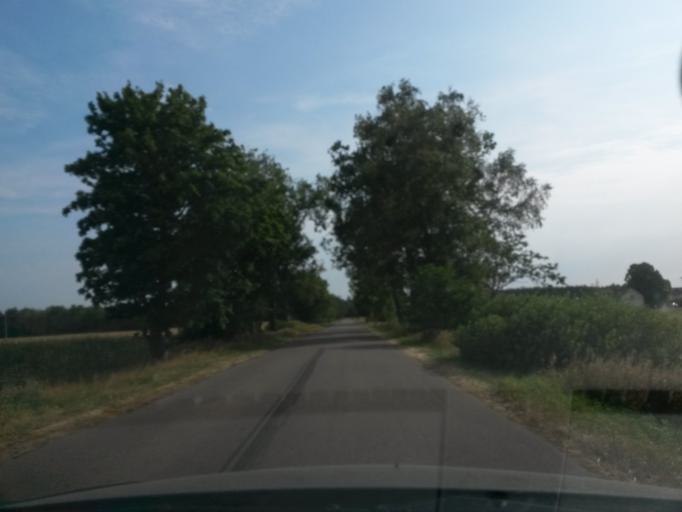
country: PL
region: Kujawsko-Pomorskie
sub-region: Powiat rypinski
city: Skrwilno
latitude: 52.9689
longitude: 19.6271
